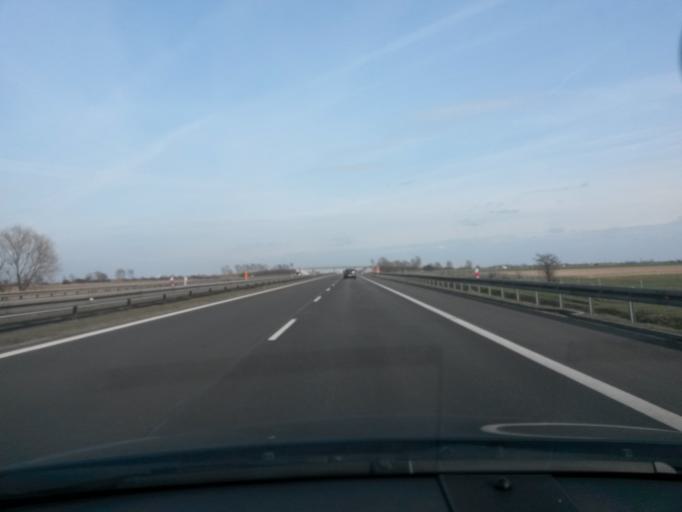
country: PL
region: Greater Poland Voivodeship
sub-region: Powiat slupecki
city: Ladek
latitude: 52.2139
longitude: 17.9802
